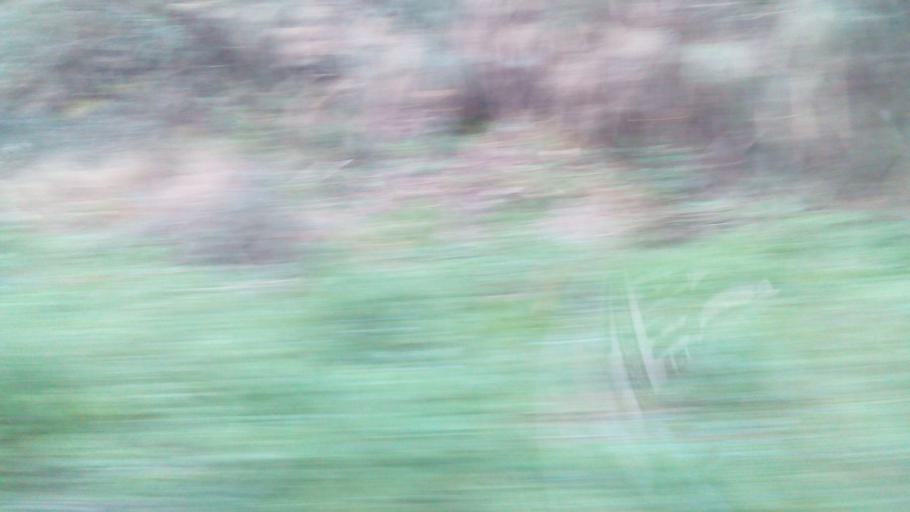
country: TW
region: Taiwan
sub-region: Hualien
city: Hualian
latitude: 24.3678
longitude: 121.3381
